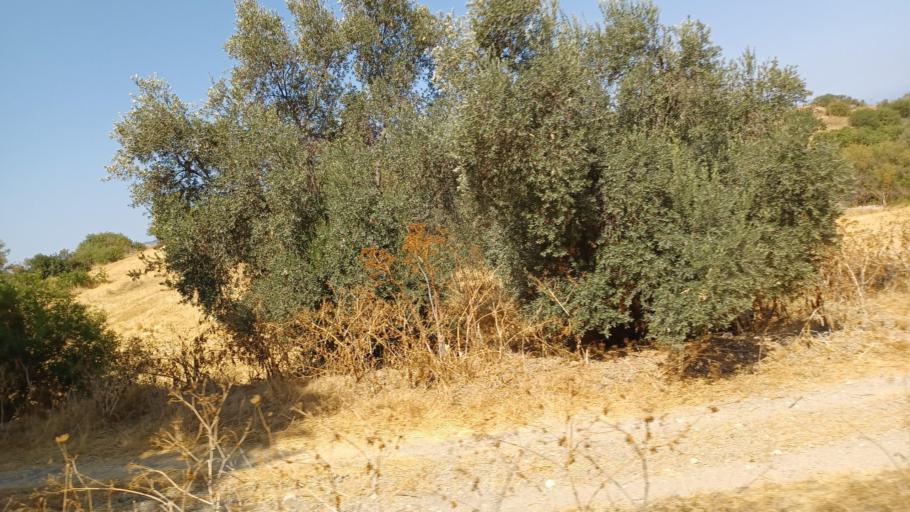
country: CY
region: Pafos
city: Polis
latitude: 34.9820
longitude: 32.4886
